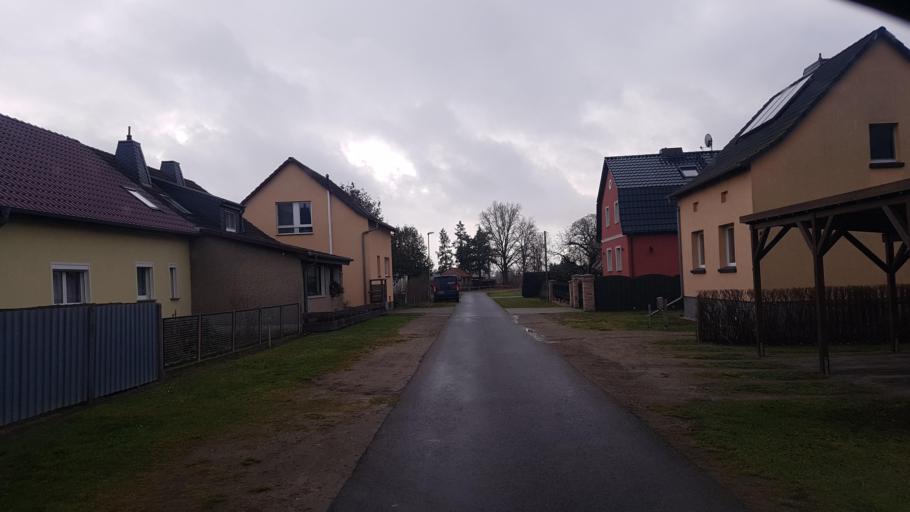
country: DE
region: Brandenburg
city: Roskow
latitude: 52.4108
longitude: 12.6891
